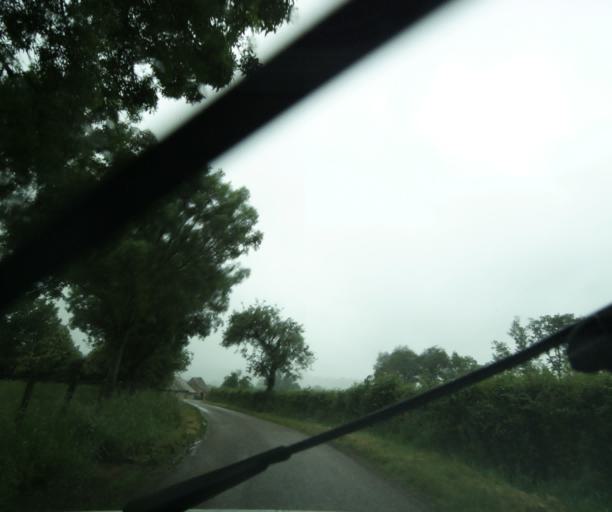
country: FR
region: Bourgogne
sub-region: Departement de Saone-et-Loire
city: Paray-le-Monial
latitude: 46.3655
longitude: 4.1832
